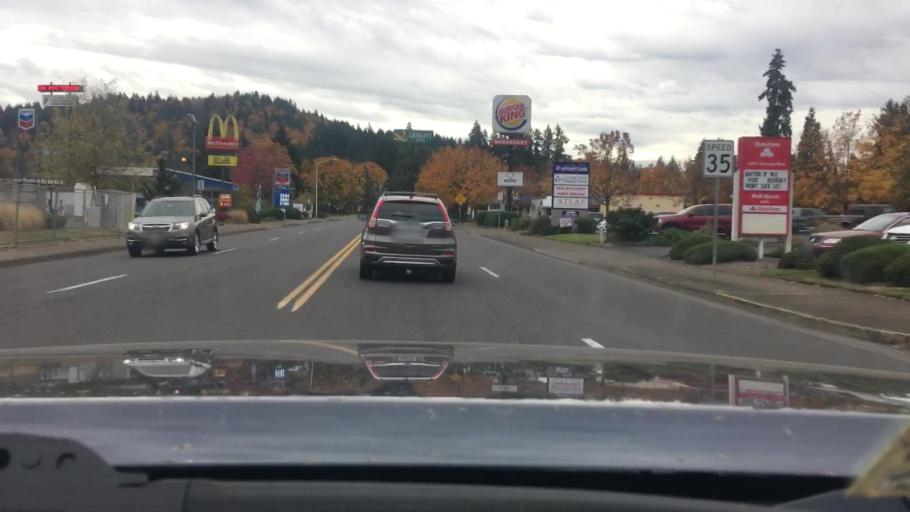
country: US
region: Oregon
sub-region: Lane County
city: Cottage Grove
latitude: 43.8038
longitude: -123.0454
